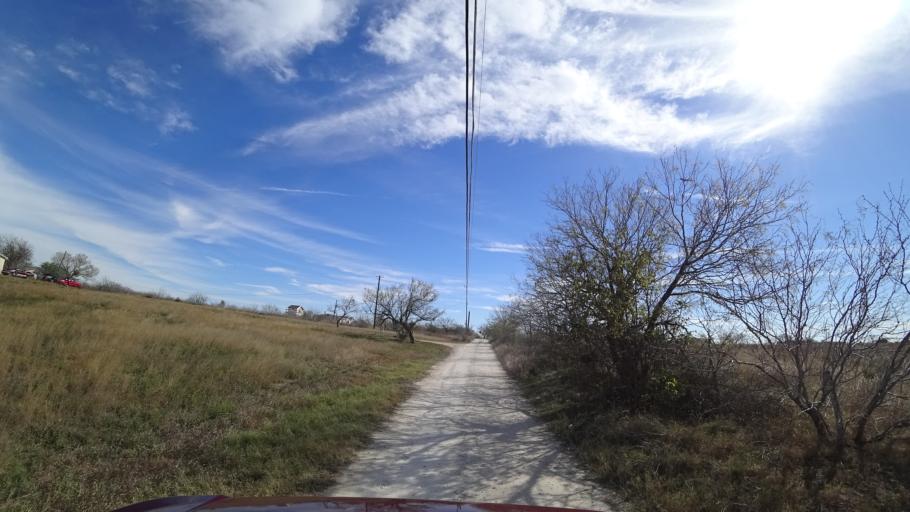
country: US
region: Texas
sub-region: Travis County
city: Onion Creek
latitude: 30.1168
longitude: -97.6844
